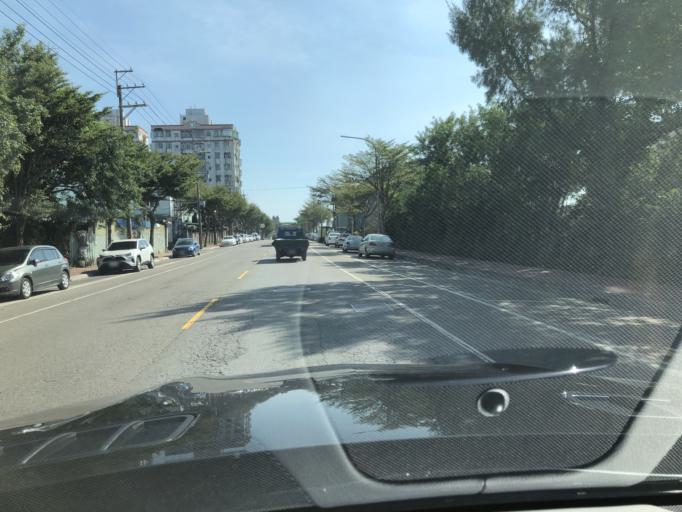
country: TW
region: Taiwan
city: Taoyuan City
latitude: 25.0684
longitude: 121.2897
